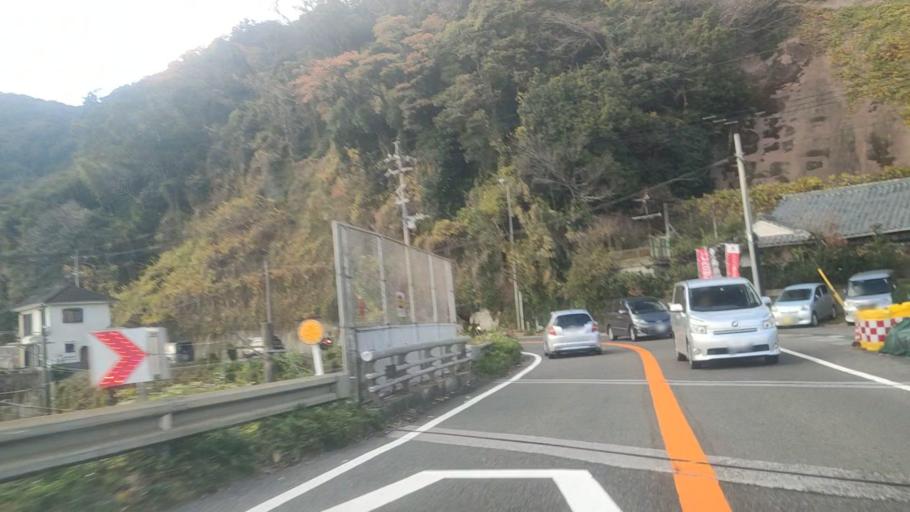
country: JP
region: Kagoshima
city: Kagoshima-shi
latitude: 31.6243
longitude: 130.5883
